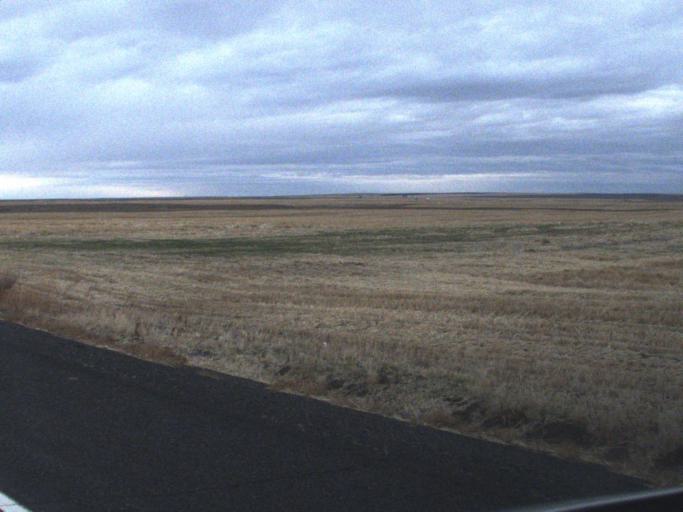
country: US
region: Washington
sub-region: Adams County
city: Ritzville
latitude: 46.7955
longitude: -118.4688
